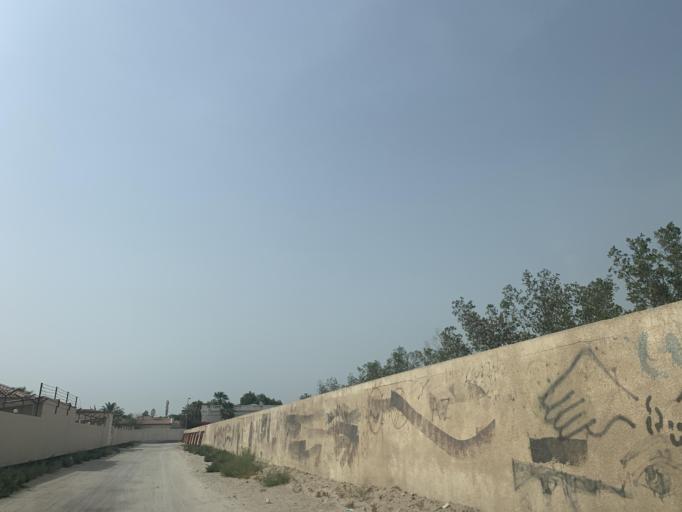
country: BH
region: Manama
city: Jidd Hafs
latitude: 26.2028
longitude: 50.4814
